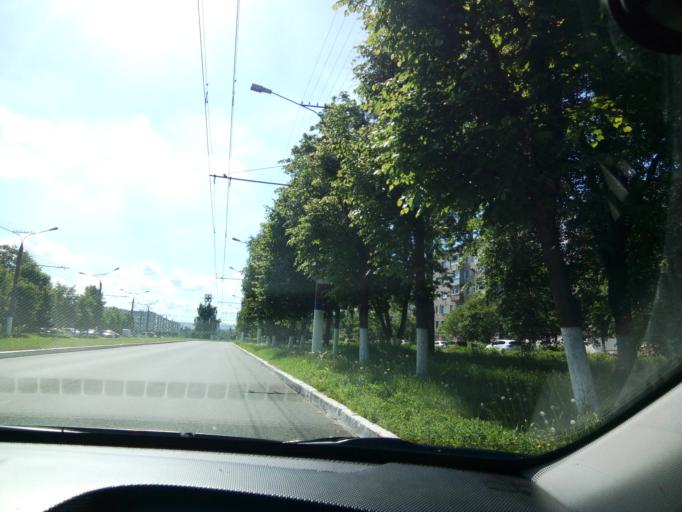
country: RU
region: Chuvashia
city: Novocheboksarsk
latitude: 56.1155
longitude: 47.4840
